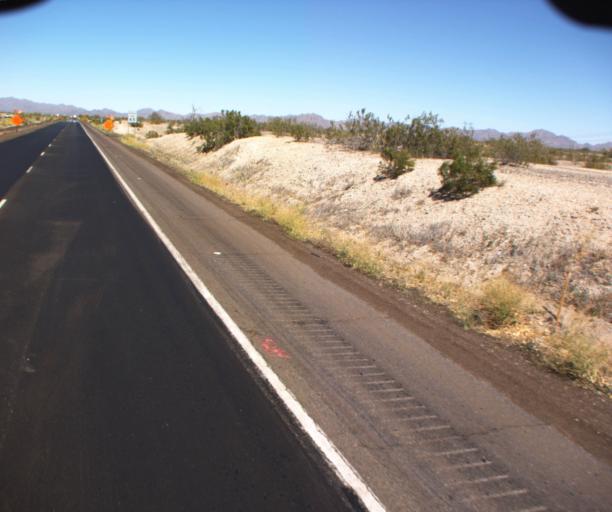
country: US
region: Arizona
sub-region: Maricopa County
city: Gila Bend
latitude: 32.9761
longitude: -112.6704
